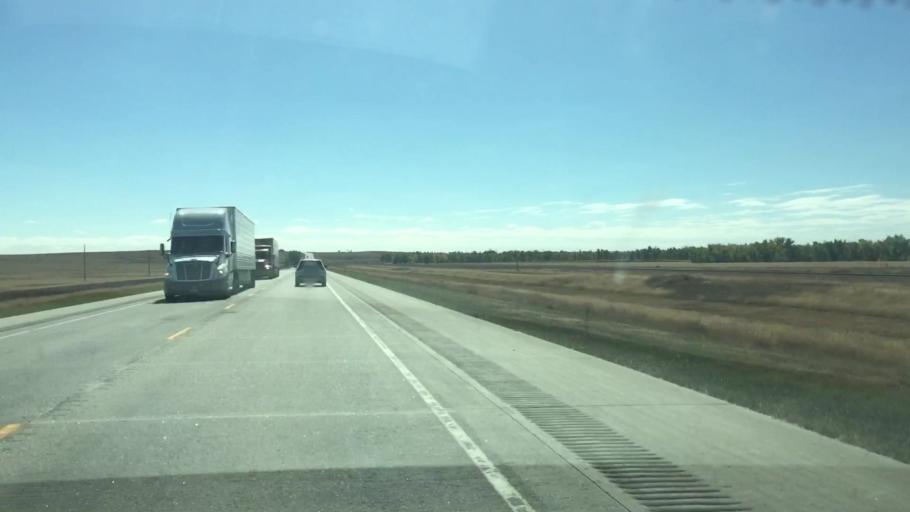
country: US
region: Colorado
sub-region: Lincoln County
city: Limon
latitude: 39.2276
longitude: -103.6135
